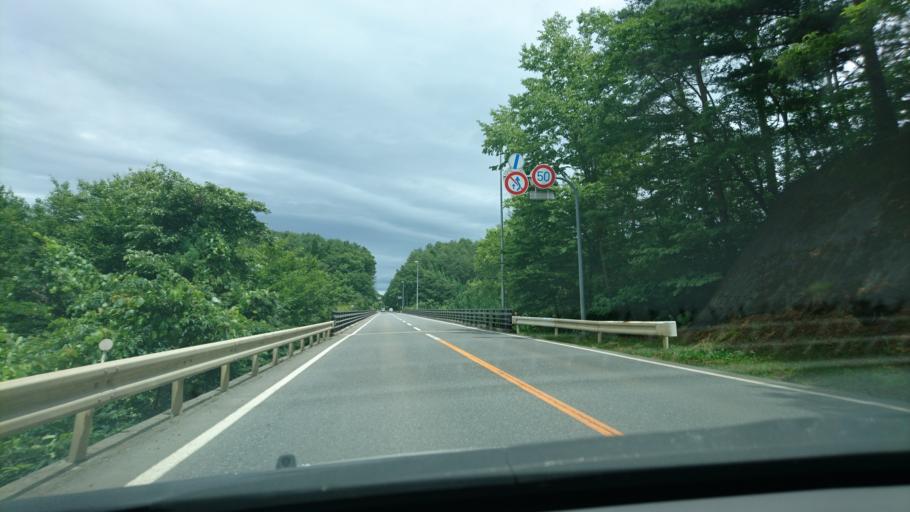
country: JP
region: Iwate
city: Miyako
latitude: 39.7081
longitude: 141.9633
